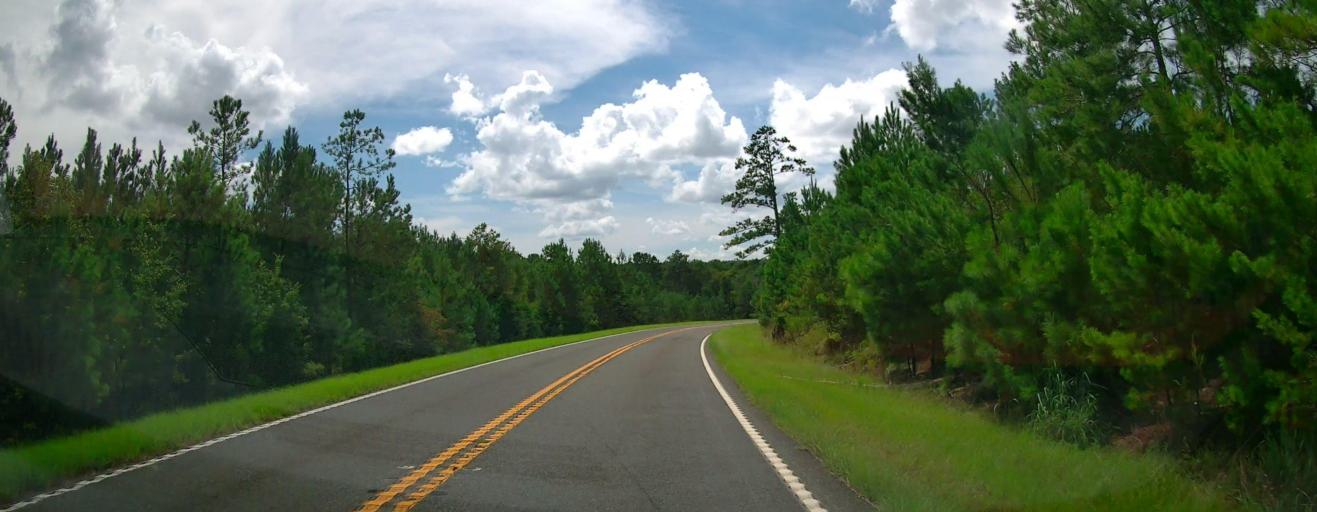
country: US
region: Georgia
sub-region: Taylor County
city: Reynolds
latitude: 32.4381
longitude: -84.1490
